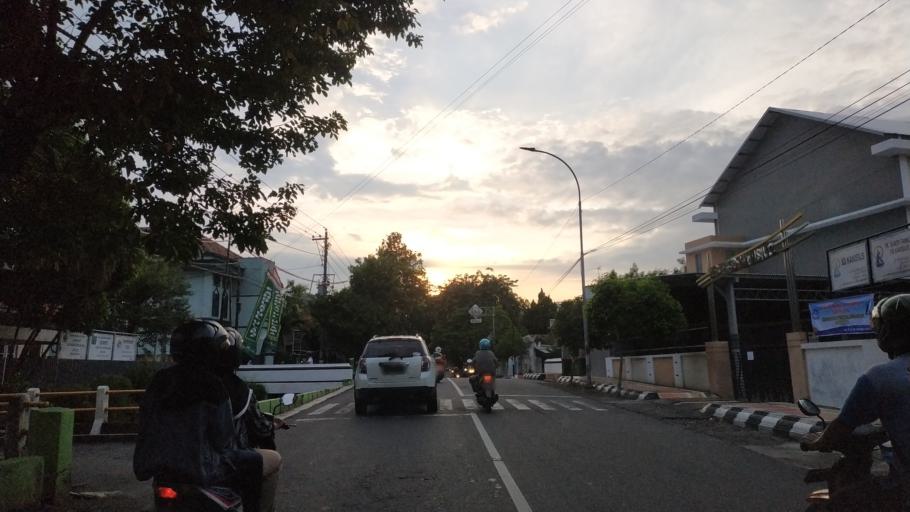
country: ID
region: Central Java
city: Kudus
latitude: -6.8111
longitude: 110.8496
